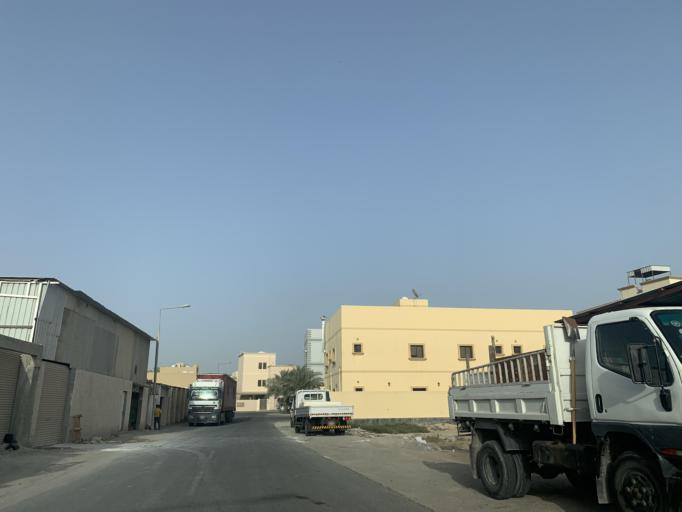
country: BH
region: Northern
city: Madinat `Isa
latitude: 26.1603
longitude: 50.5110
